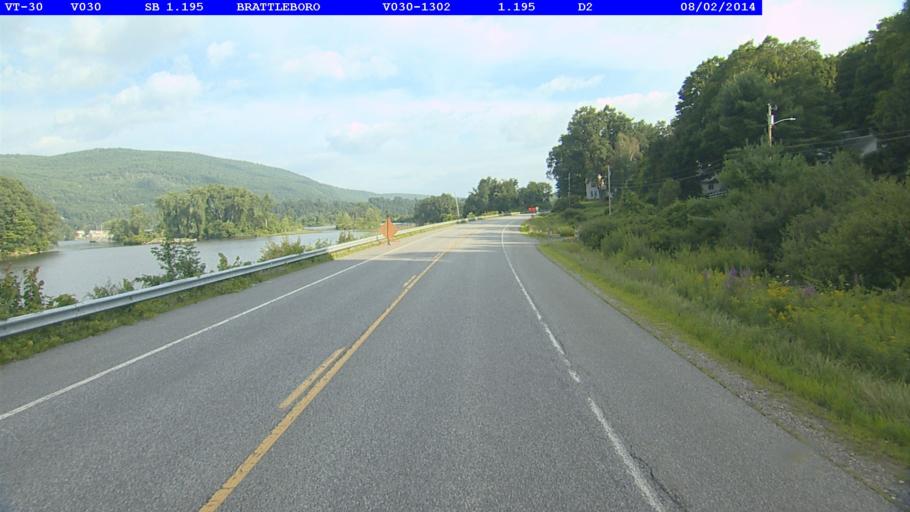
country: US
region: Vermont
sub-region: Windham County
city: Brattleboro
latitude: 42.8726
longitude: -72.5703
